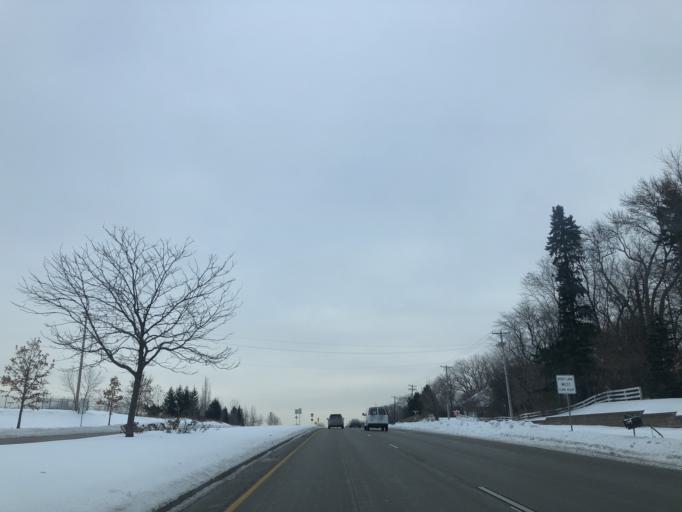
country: US
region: Minnesota
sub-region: Ramsey County
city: Shoreview
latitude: 45.0792
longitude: -93.1650
